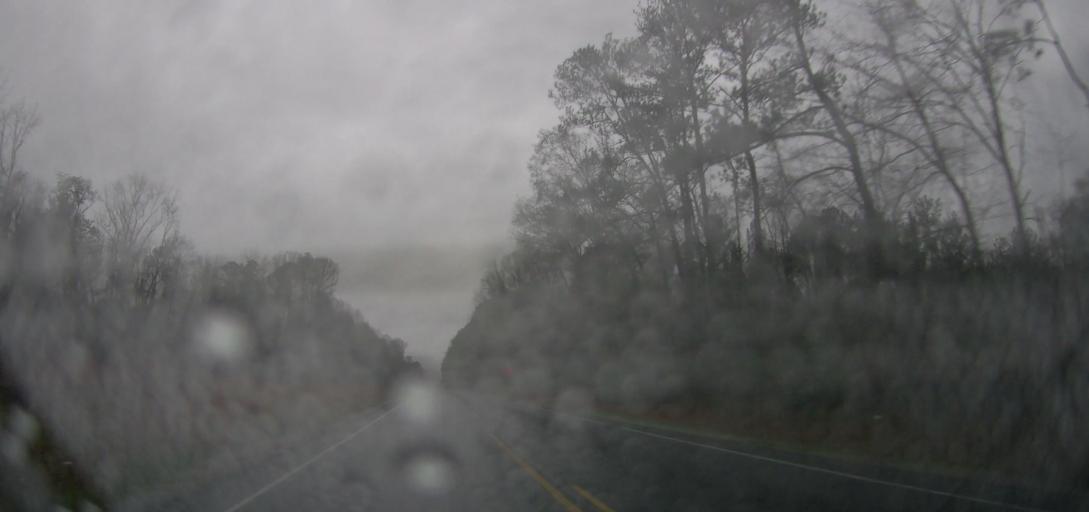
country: US
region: Alabama
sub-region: Chilton County
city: Clanton
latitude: 32.6079
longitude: -86.7160
